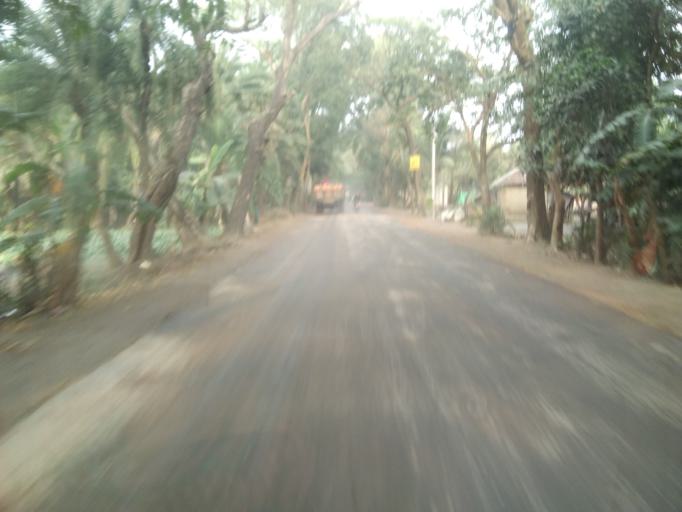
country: BD
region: Khulna
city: Satkhira
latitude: 22.6778
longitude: 89.0197
